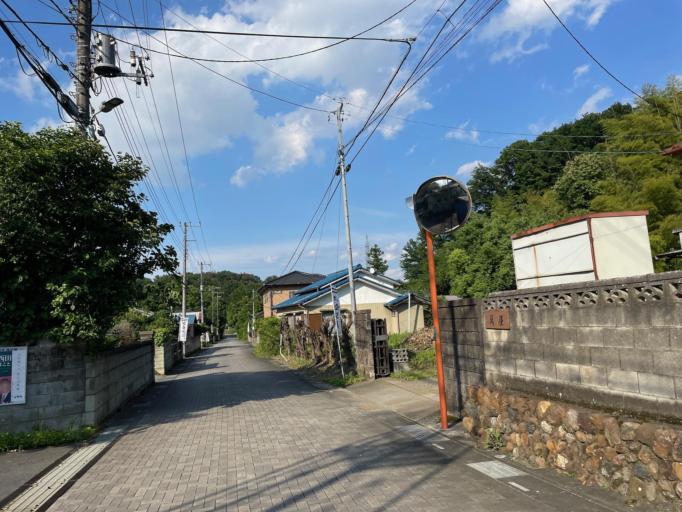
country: JP
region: Saitama
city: Sakado
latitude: 36.0046
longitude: 139.3672
